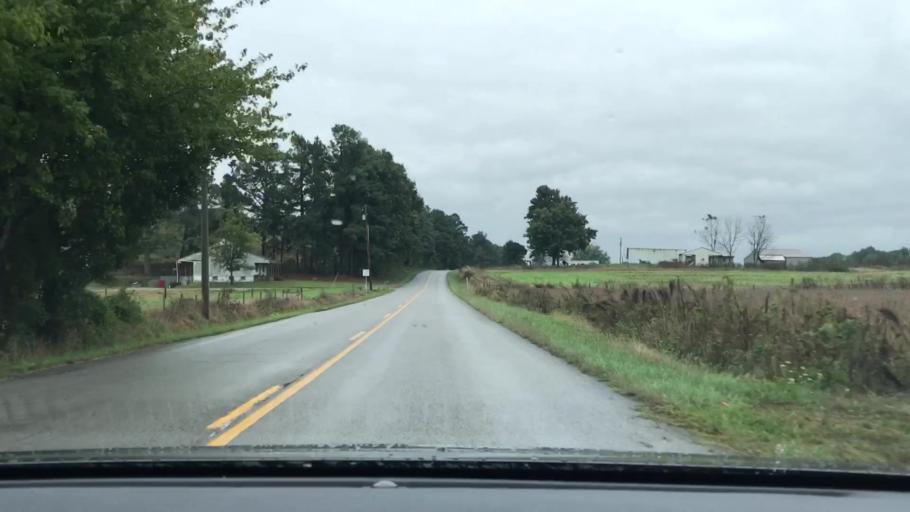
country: US
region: Kentucky
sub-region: McLean County
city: Calhoun
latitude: 37.4823
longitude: -87.2468
